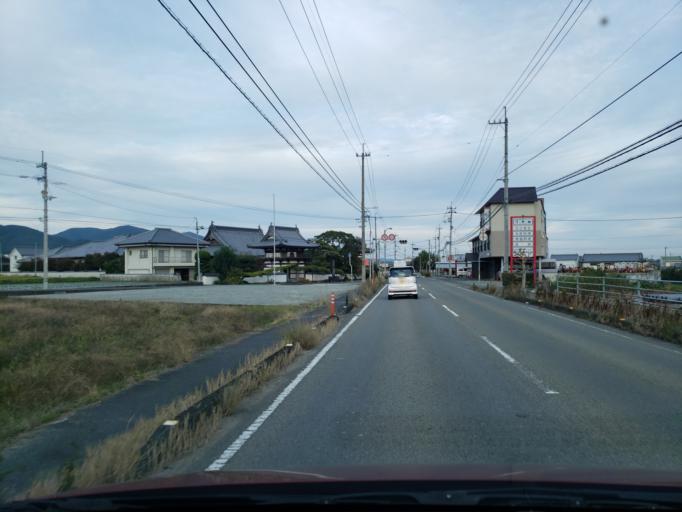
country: JP
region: Tokushima
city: Kamojimacho-jogejima
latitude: 34.0964
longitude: 134.3191
